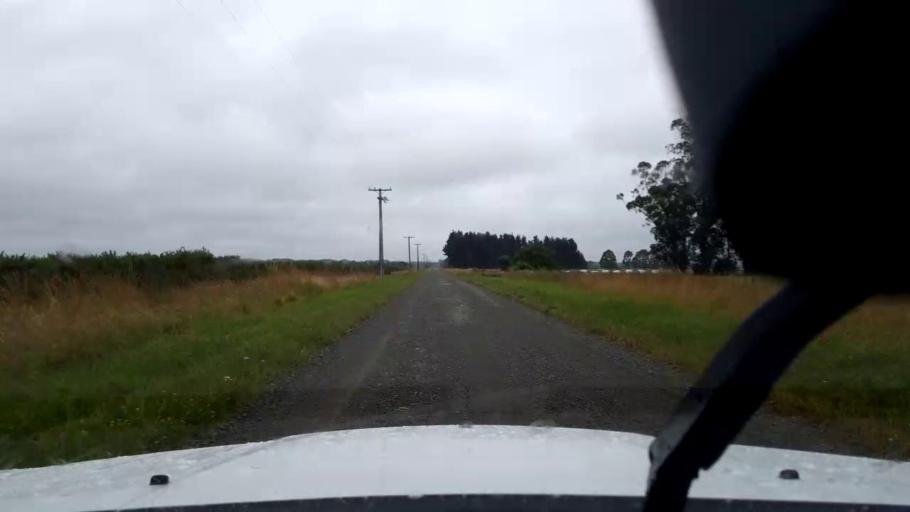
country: NZ
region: Canterbury
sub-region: Timaru District
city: Pleasant Point
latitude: -44.2375
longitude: 171.2020
